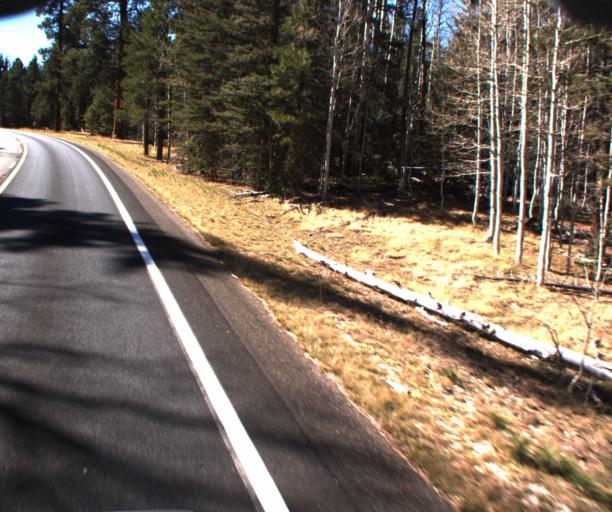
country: US
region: Arizona
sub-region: Coconino County
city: Grand Canyon
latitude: 36.5073
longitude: -112.1401
